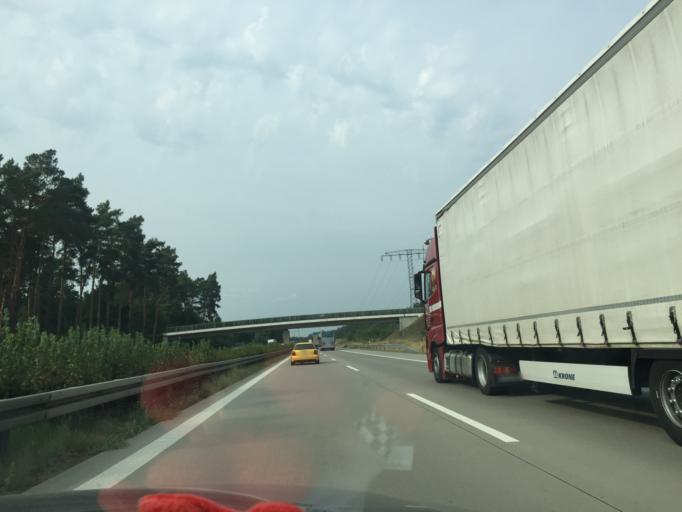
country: DE
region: Brandenburg
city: Schwerin
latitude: 52.1410
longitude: 13.6485
